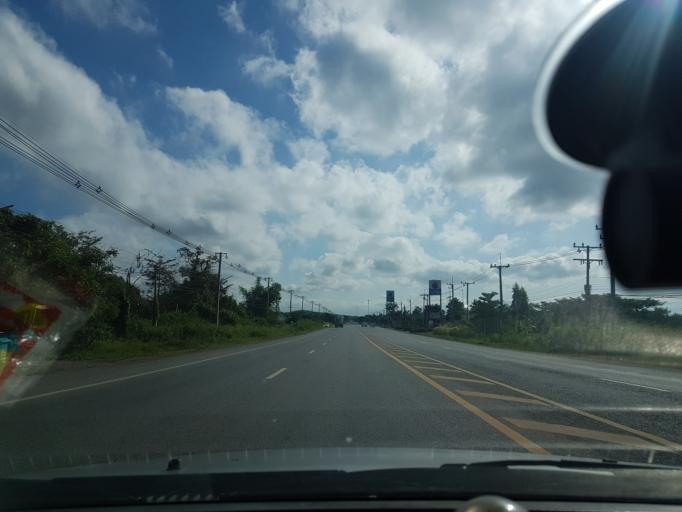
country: TH
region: Lop Buri
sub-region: Amphoe Tha Luang
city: Tha Luang
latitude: 15.0793
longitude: 101.0294
